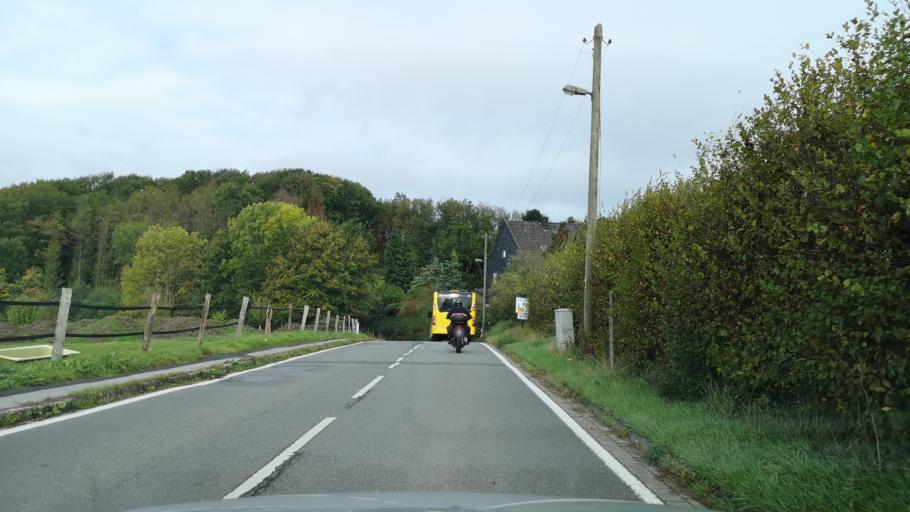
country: DE
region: North Rhine-Westphalia
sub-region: Regierungsbezirk Dusseldorf
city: Velbert
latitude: 51.3834
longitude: 7.0479
